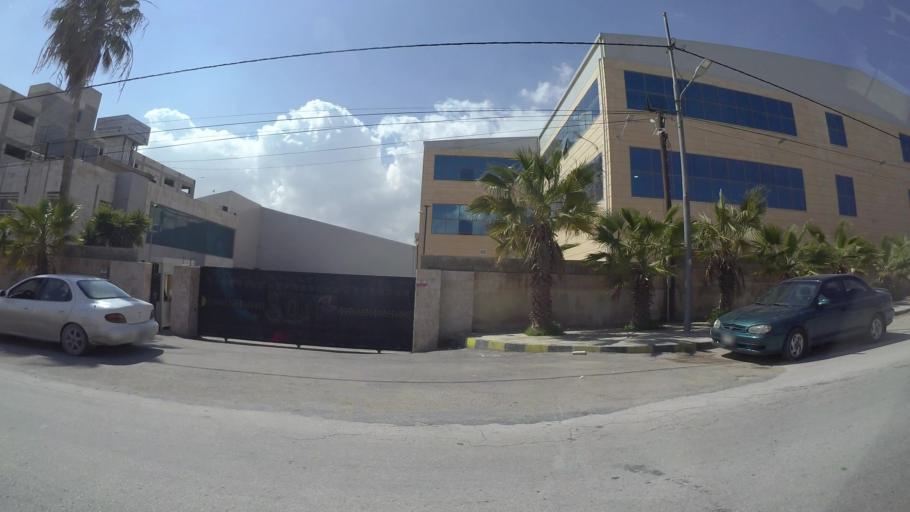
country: JO
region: Zarqa
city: Russeifa
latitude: 31.9948
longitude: 36.0113
